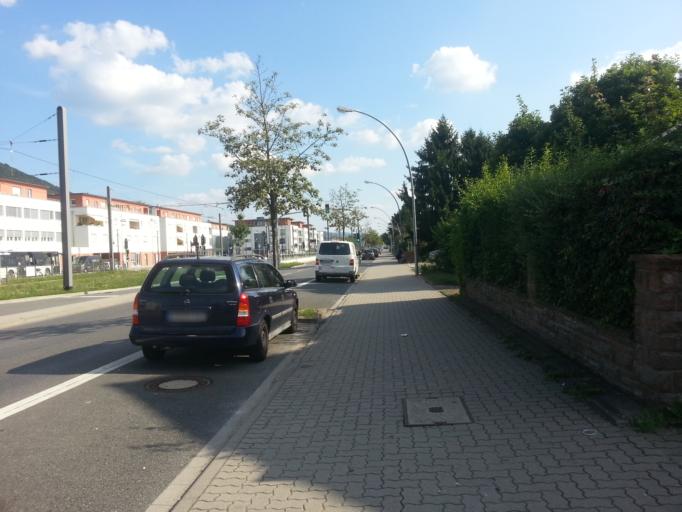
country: DE
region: Baden-Wuerttemberg
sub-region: Karlsruhe Region
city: Schriesheim
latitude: 49.4728
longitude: 8.6595
